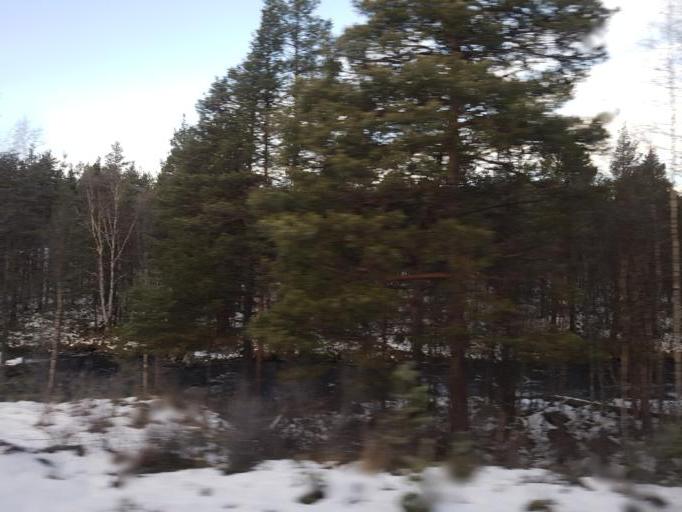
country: NO
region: Sor-Trondelag
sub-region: Rennebu
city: Berkak
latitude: 62.6997
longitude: 9.9994
